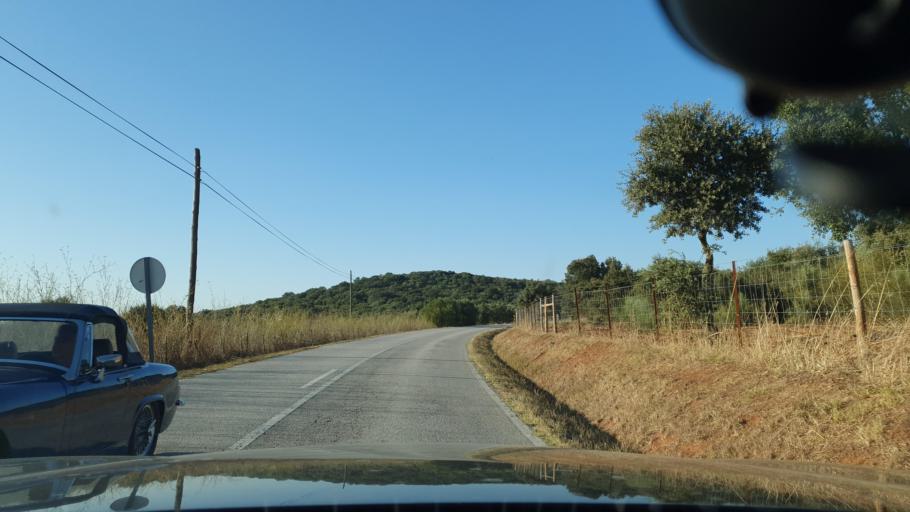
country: PT
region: Evora
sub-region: Estremoz
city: Estremoz
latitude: 38.9025
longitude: -7.6680
